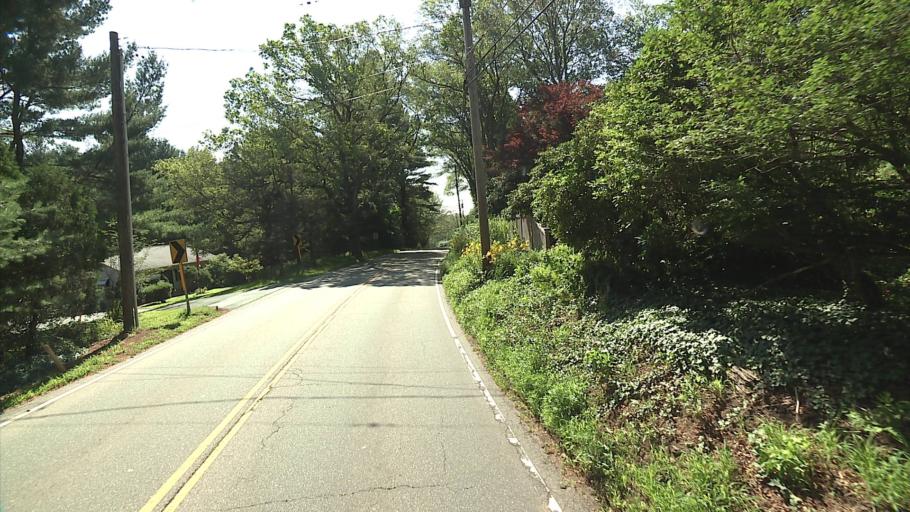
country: US
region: Connecticut
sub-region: Windham County
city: Windham
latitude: 41.7146
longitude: -72.1765
